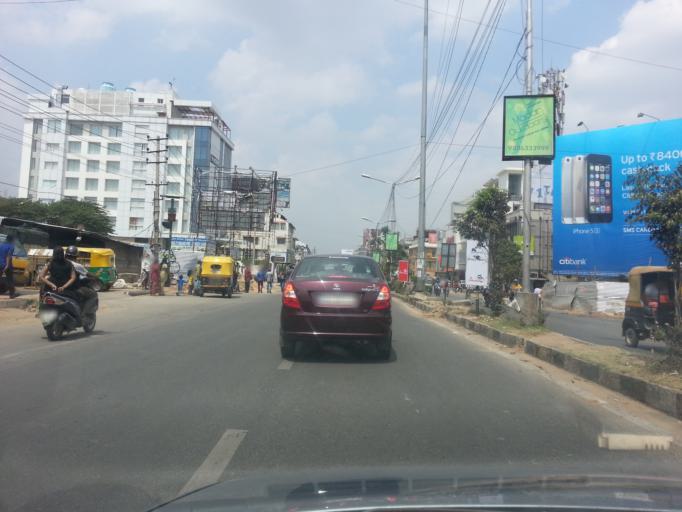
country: IN
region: Karnataka
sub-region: Bangalore Urban
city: Bangalore
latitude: 12.9545
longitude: 77.6413
